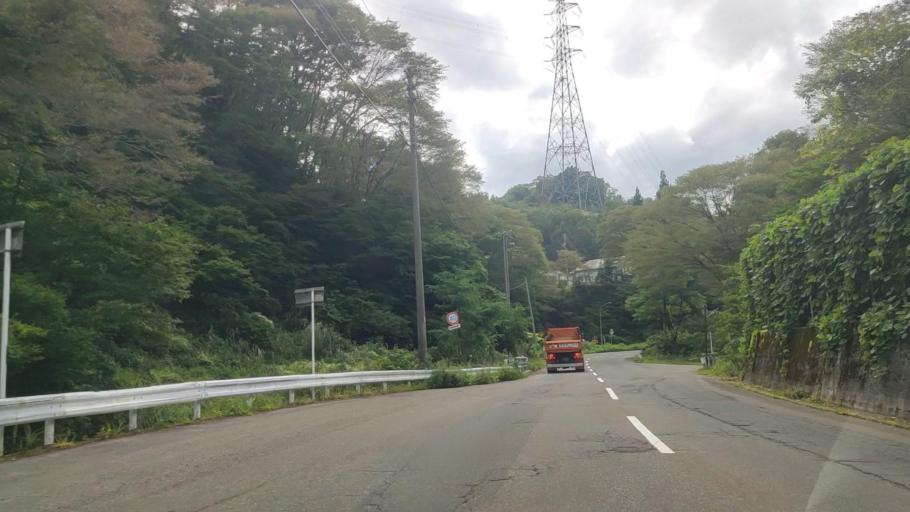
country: JP
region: Nagano
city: Iiyama
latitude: 36.8913
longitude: 138.3235
